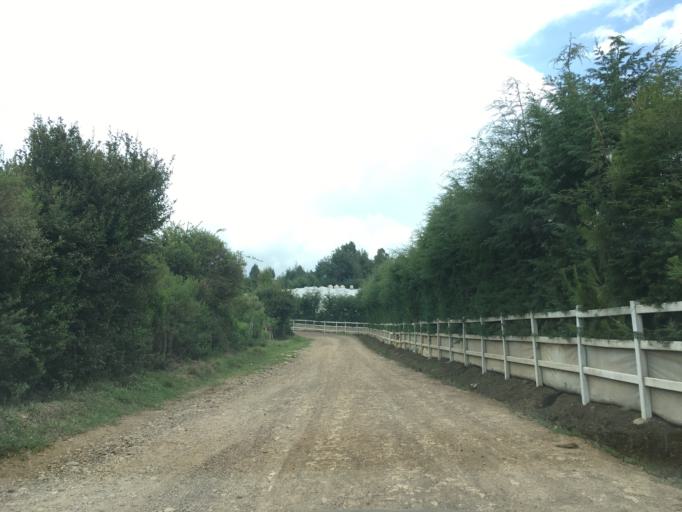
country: MX
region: Michoacan
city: Acuitzio del Canje
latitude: 19.4924
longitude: -101.2358
